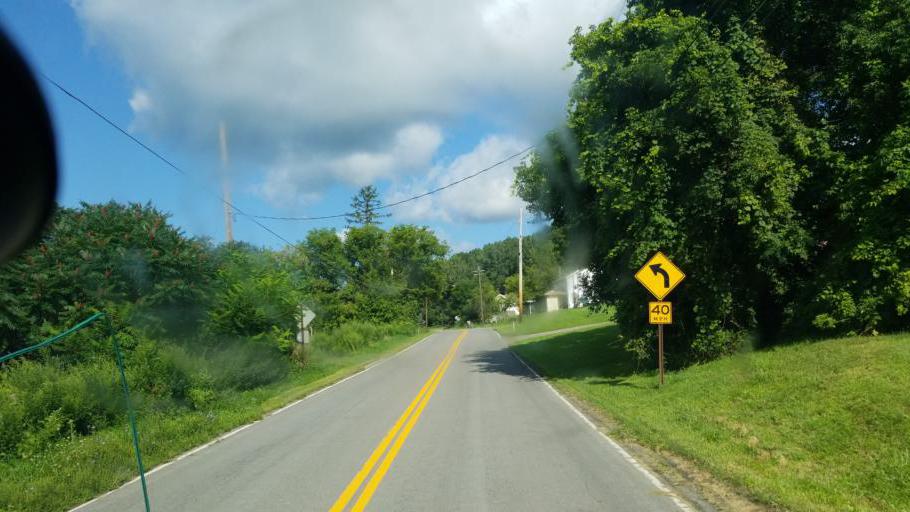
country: US
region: New York
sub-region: Steuben County
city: Canisteo
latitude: 42.2850
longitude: -77.6058
